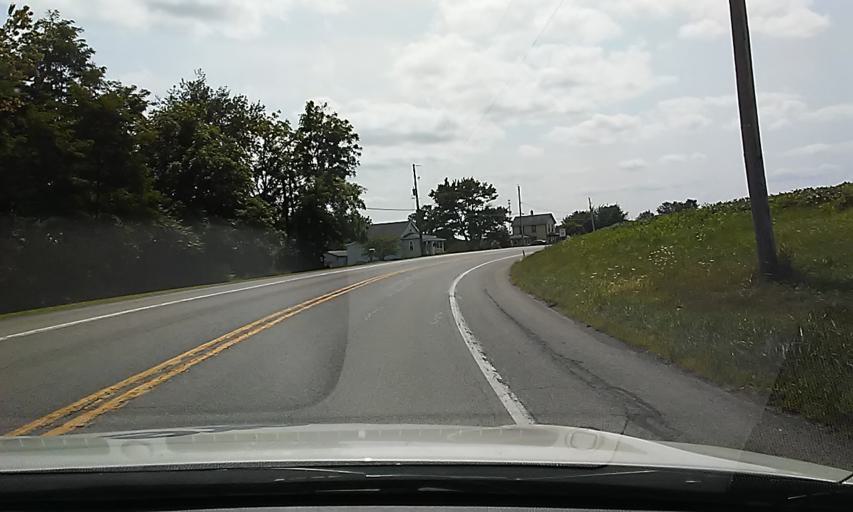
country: US
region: Pennsylvania
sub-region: Jefferson County
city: Punxsutawney
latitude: 40.8551
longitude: -79.0241
